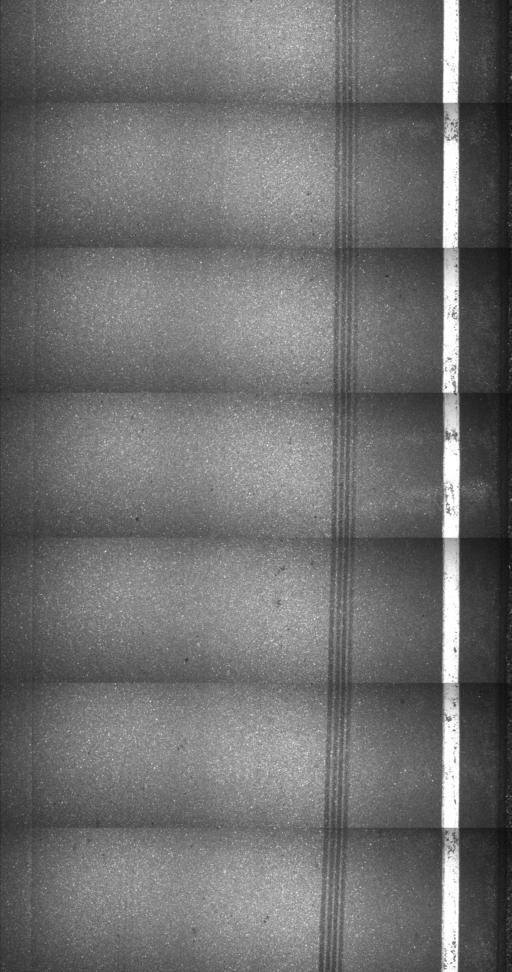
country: US
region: Vermont
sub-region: Caledonia County
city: Lyndonville
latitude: 44.7063
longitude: -72.0124
